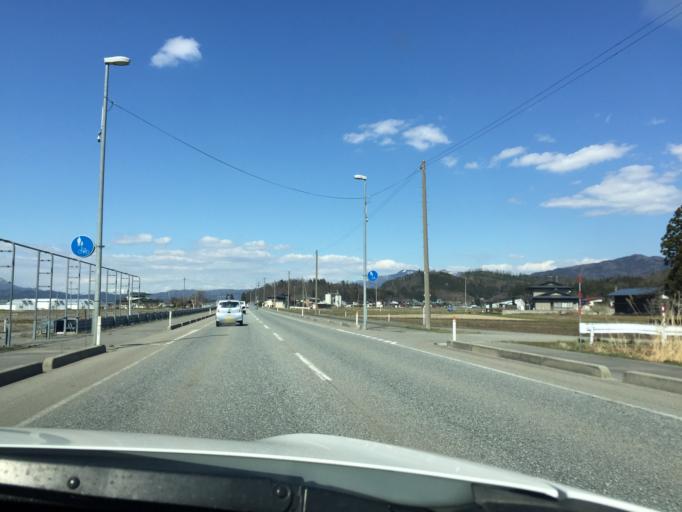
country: JP
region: Yamagata
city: Nagai
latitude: 38.1423
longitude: 140.0591
